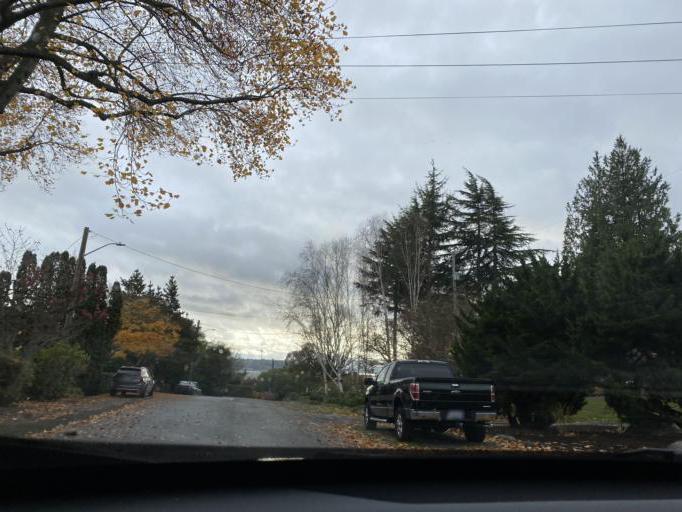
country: US
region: Washington
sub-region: King County
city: Seattle
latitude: 47.6335
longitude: -122.3902
